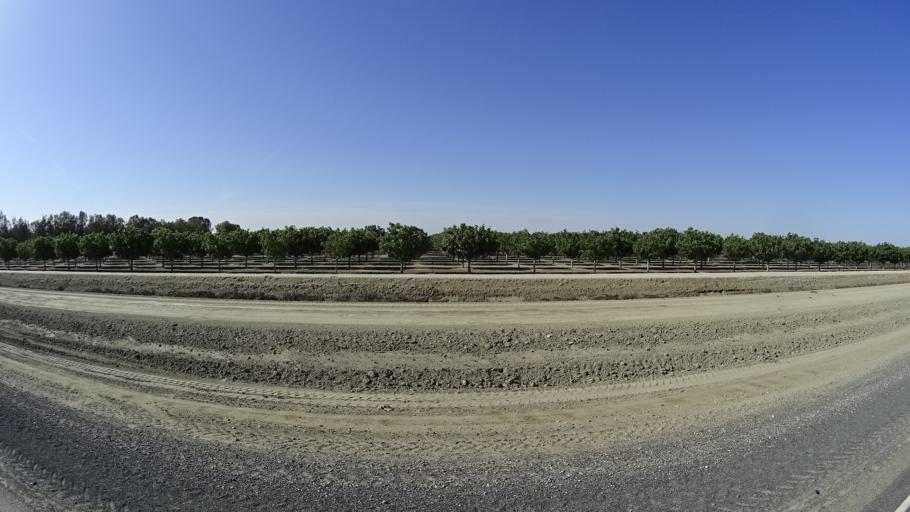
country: US
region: California
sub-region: Kings County
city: Corcoran
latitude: 36.0981
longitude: -119.5969
